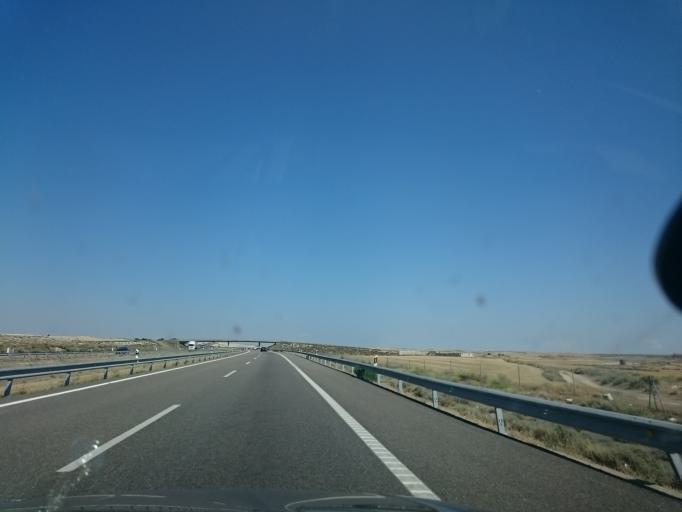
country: ES
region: Aragon
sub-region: Provincia de Zaragoza
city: Bujaraloz
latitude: 41.5178
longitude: -0.2336
